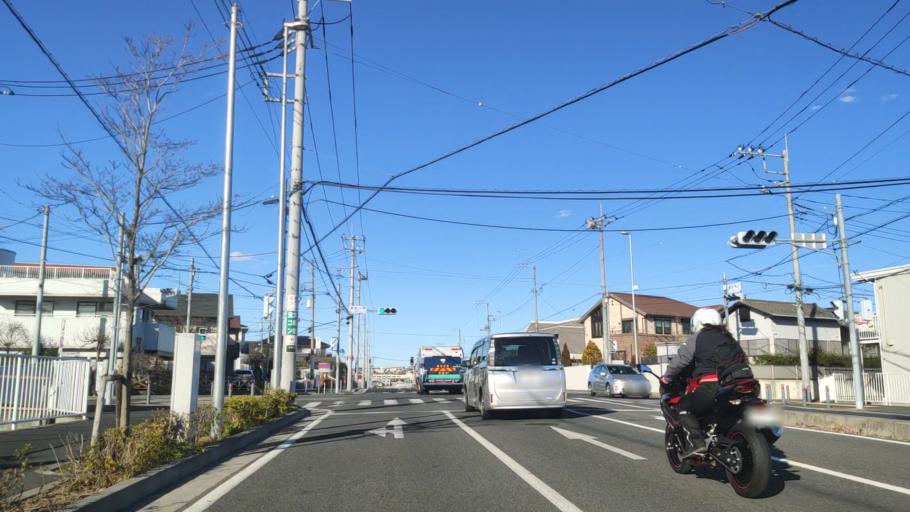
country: JP
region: Tokyo
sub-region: Machida-shi
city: Machida
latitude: 35.5199
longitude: 139.5444
